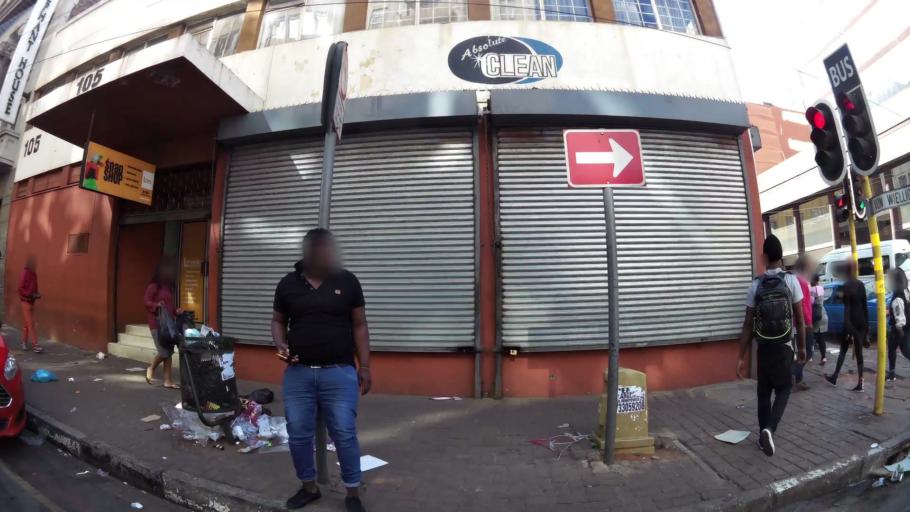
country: ZA
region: Gauteng
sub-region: City of Johannesburg Metropolitan Municipality
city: Johannesburg
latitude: -26.2040
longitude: 28.0473
